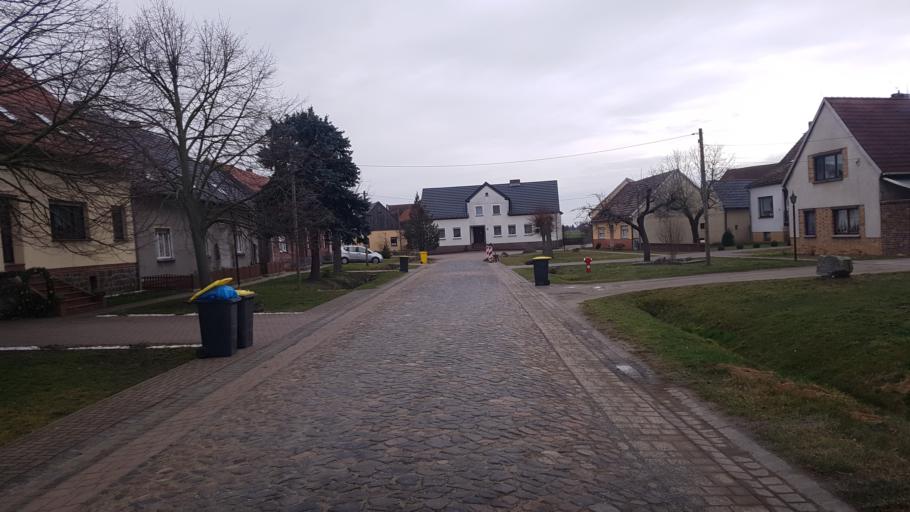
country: DE
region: Brandenburg
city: Sonnewalde
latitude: 51.7094
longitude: 13.6711
